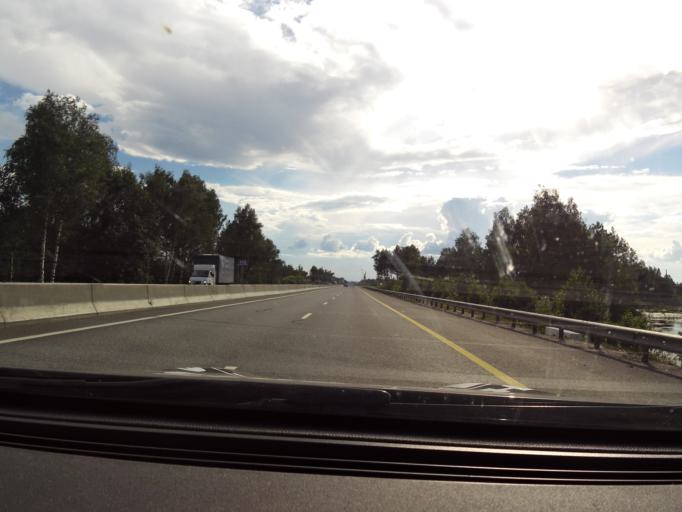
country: RU
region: Vladimir
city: Galitsy
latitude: 56.2406
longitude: 42.8410
